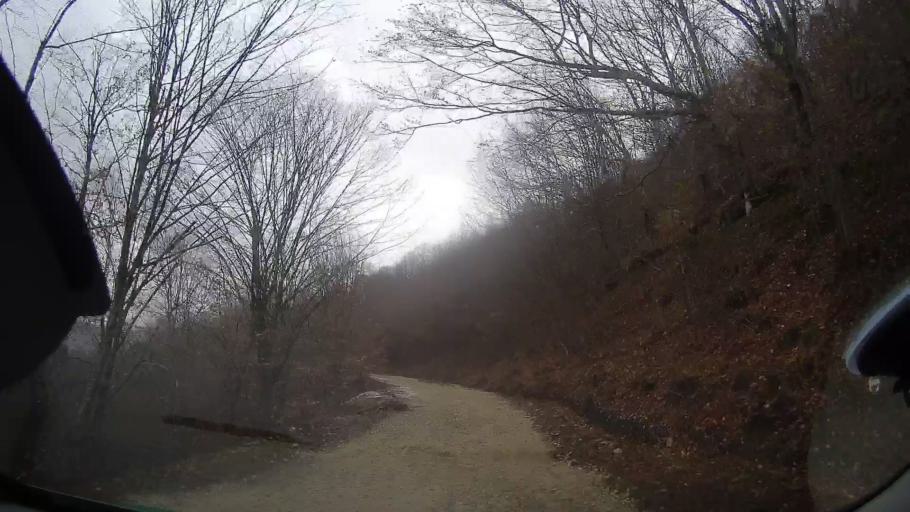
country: RO
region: Cluj
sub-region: Comuna Maguri-Racatau
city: Maguri-Racatau
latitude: 46.6530
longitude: 23.1917
